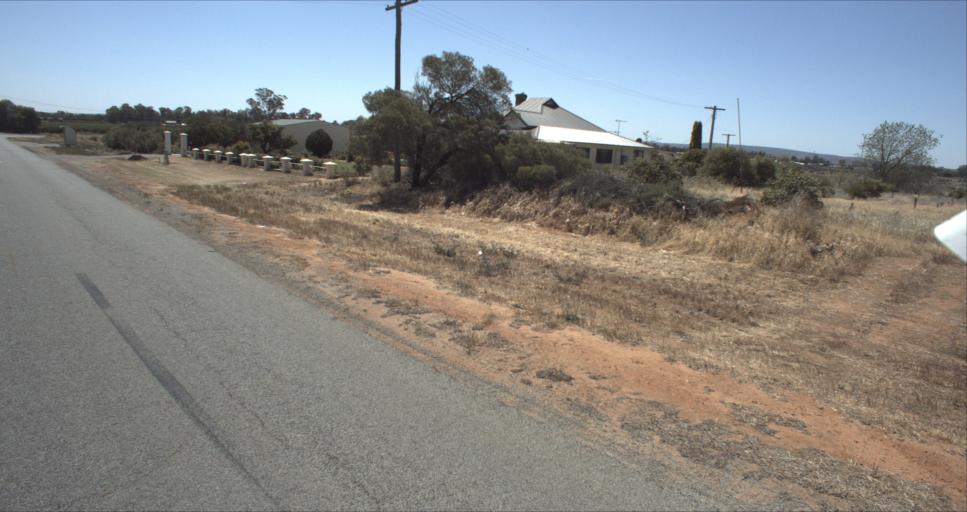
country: AU
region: New South Wales
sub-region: Leeton
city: Leeton
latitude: -34.5391
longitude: 146.3957
